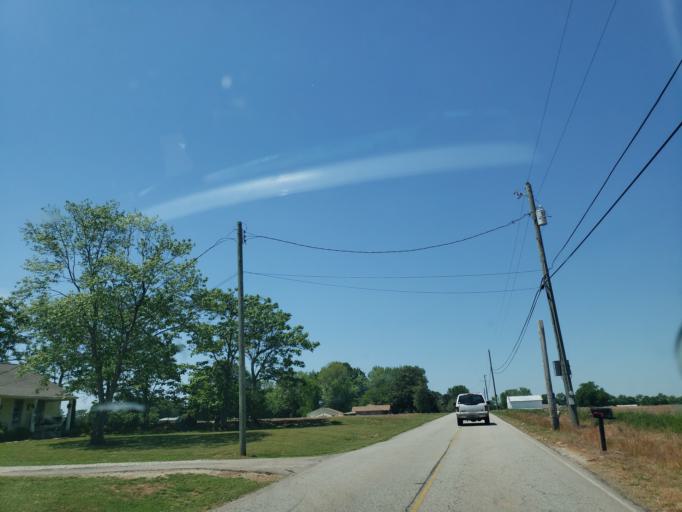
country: US
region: Alabama
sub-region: Madison County
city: Hazel Green
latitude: 34.9618
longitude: -86.6064
